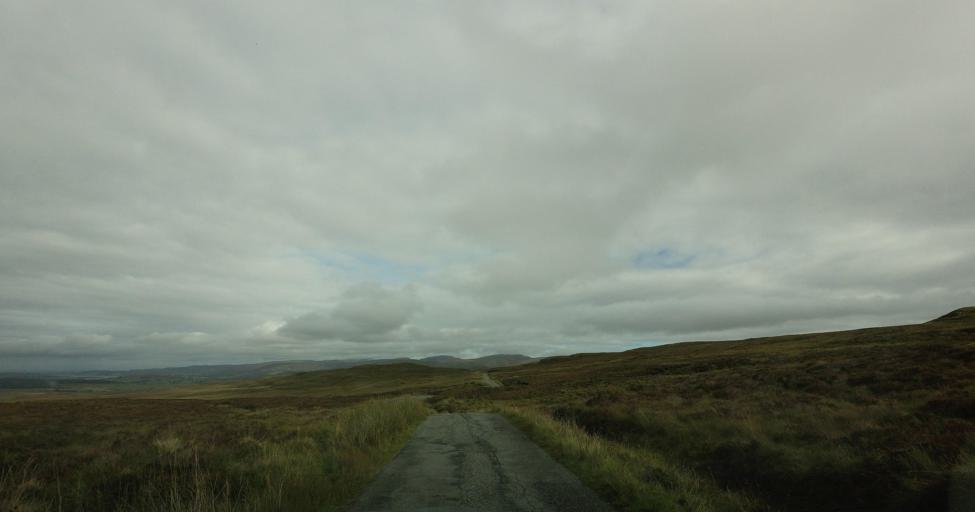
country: GB
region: Scotland
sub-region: Highland
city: Isle of Skye
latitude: 57.4022
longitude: -6.2689
